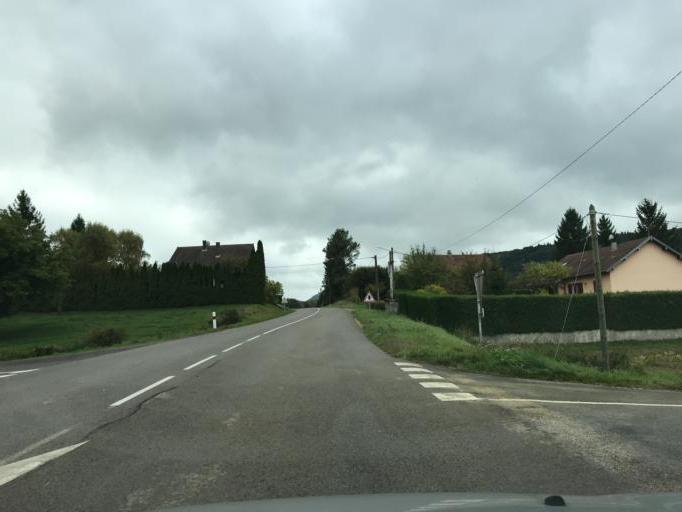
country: FR
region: Rhone-Alpes
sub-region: Departement de l'Ain
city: Cuisiat
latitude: 46.3745
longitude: 5.4385
